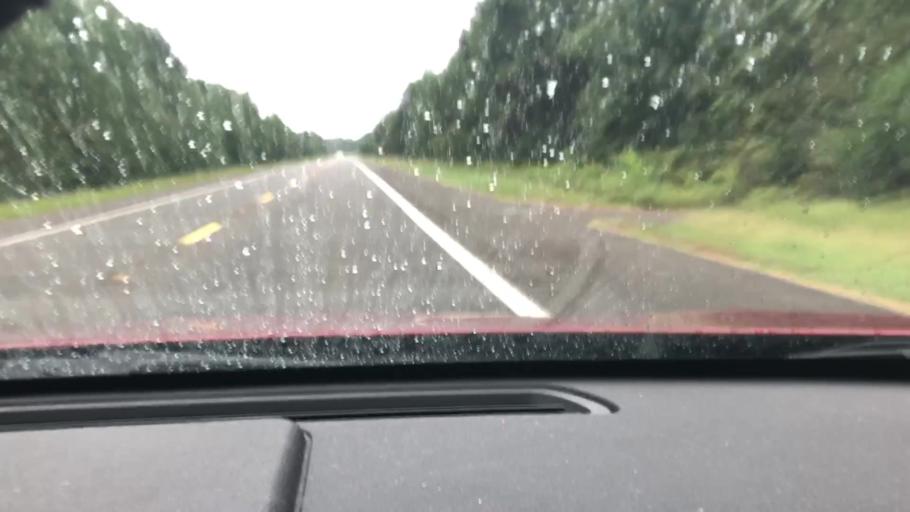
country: US
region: Arkansas
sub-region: Columbia County
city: Waldo
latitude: 33.3054
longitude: -93.2735
